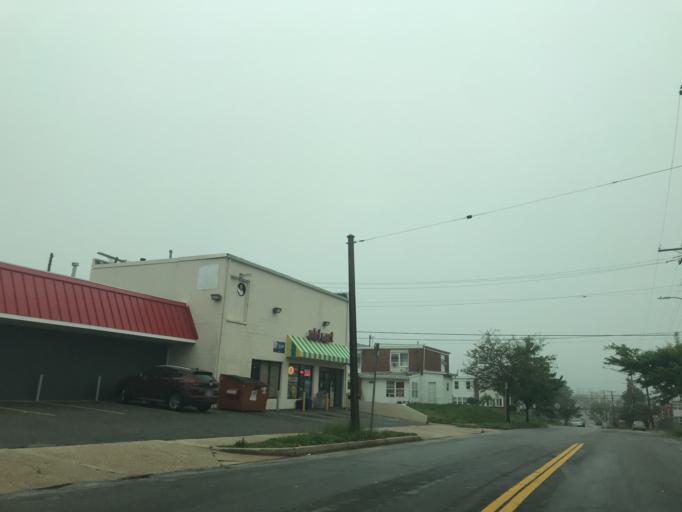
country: US
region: Maryland
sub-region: Baltimore County
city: Rosedale
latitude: 39.2950
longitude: -76.5118
